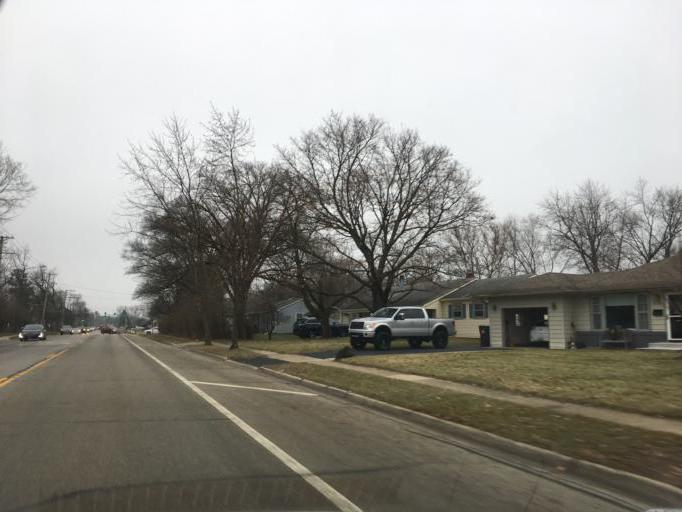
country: US
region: Illinois
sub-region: McHenry County
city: Lakewood
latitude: 42.2239
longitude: -88.3377
